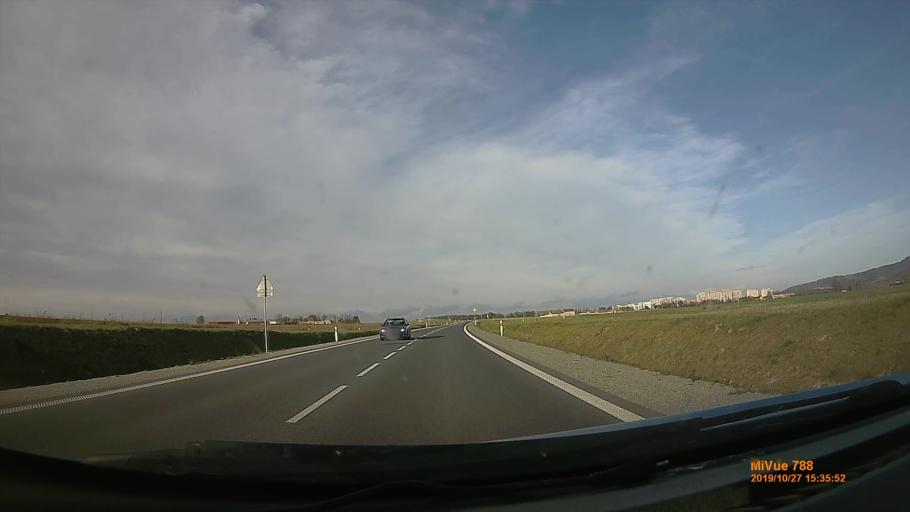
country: PL
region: Lower Silesian Voivodeship
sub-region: Powiat klodzki
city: Klodzko
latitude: 50.4207
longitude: 16.6257
